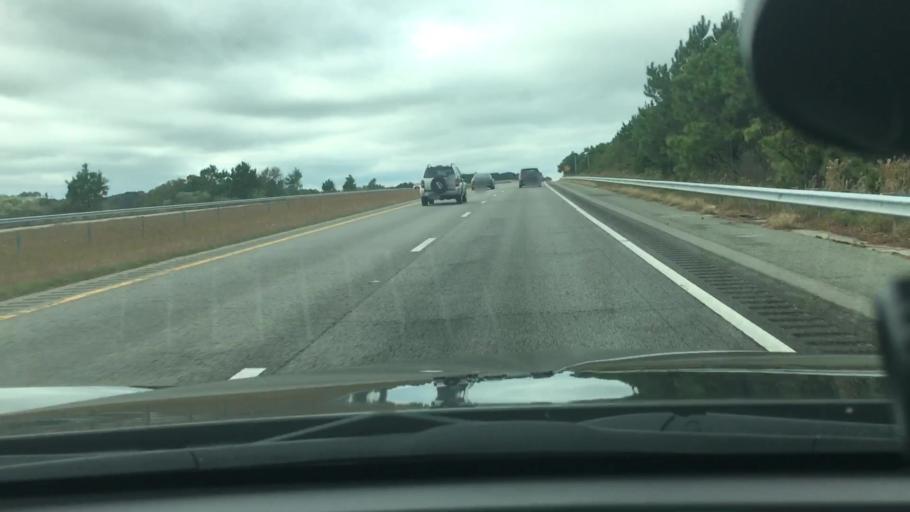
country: US
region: North Carolina
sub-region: Wilson County
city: Wilson
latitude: 35.6753
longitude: -77.9311
